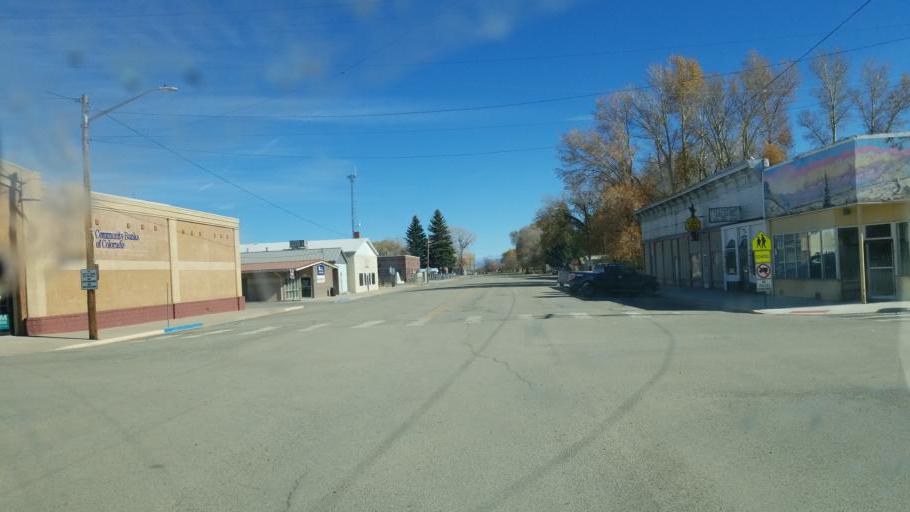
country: US
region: Colorado
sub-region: Conejos County
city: Conejos
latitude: 37.2748
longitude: -105.9593
